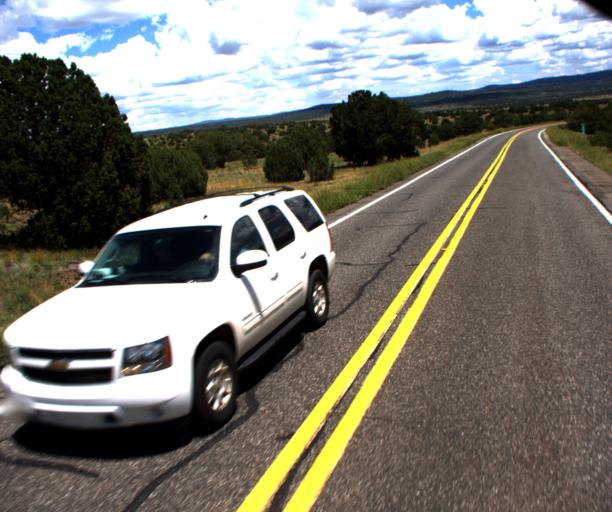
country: US
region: Arizona
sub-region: Gila County
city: Pine
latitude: 34.4870
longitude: -111.6095
